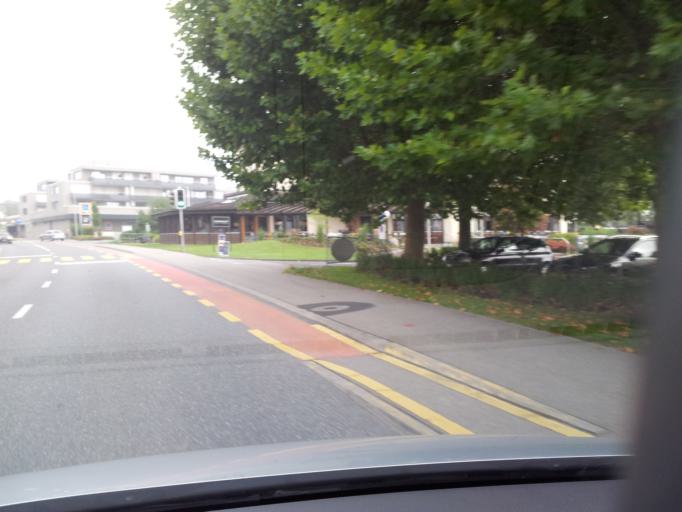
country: CH
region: Lucerne
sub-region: Hochdorf District
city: Emmen
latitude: 47.0995
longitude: 8.2689
